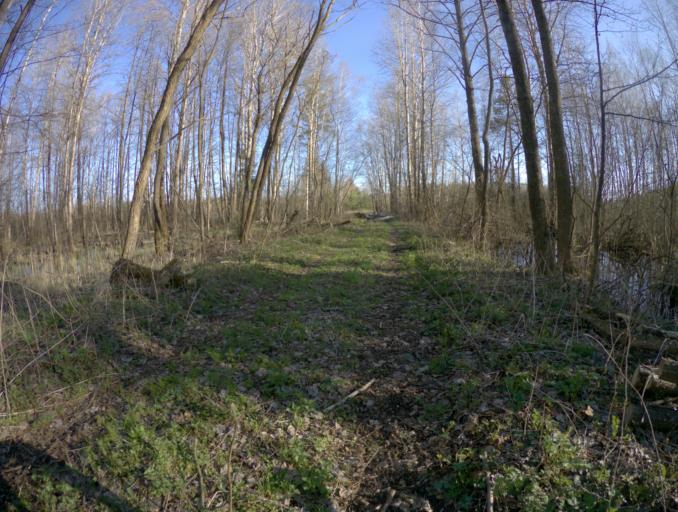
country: RU
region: Vladimir
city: Mezinovskiy
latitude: 55.6215
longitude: 40.3835
